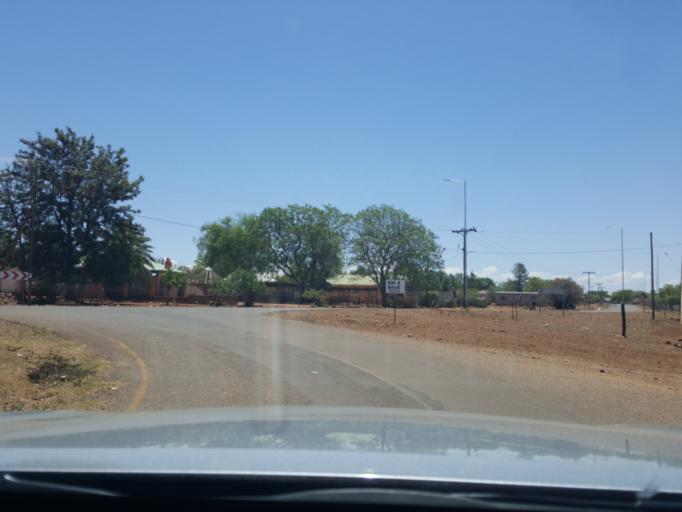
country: BW
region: South East
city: Ramotswa
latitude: -24.8709
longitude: 25.8799
